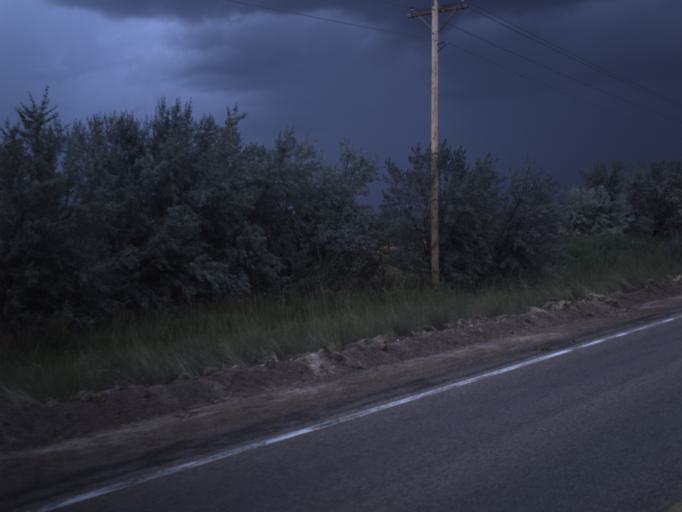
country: US
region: Utah
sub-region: Duchesne County
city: Roosevelt
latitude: 40.3869
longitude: -110.0298
